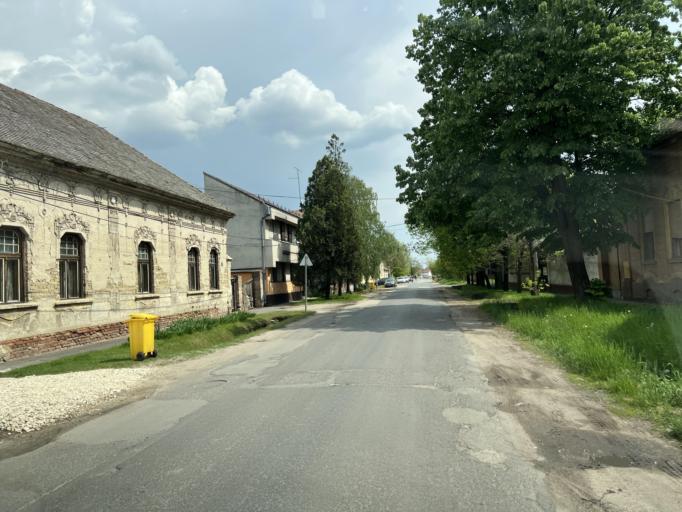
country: HU
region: Pest
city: Nagykoros
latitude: 47.0277
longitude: 19.7836
